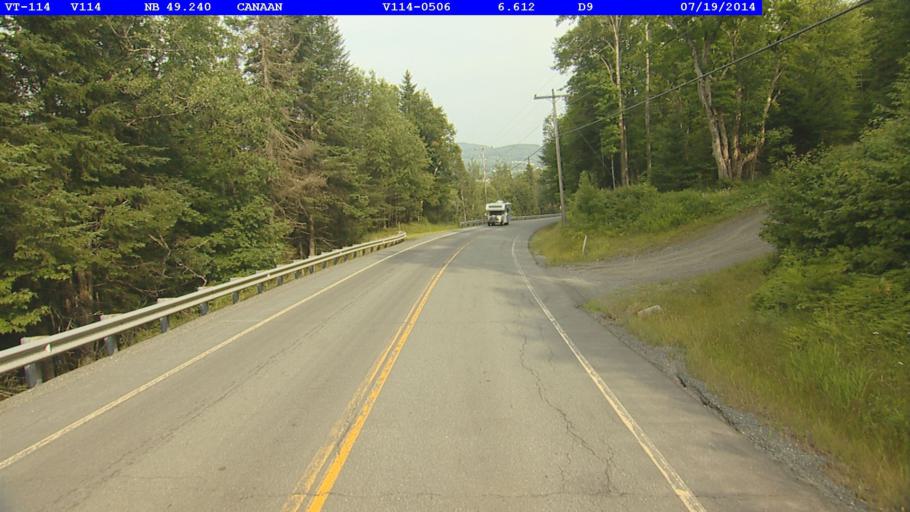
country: US
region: New Hampshire
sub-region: Coos County
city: Colebrook
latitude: 45.0093
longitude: -71.5638
